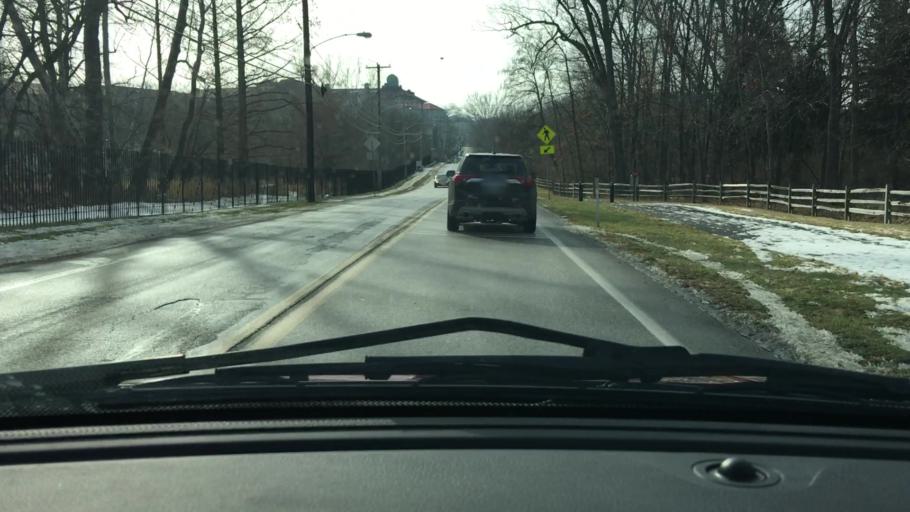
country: US
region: Pennsylvania
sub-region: Montgomery County
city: Flourtown
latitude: 40.0903
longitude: -75.2263
